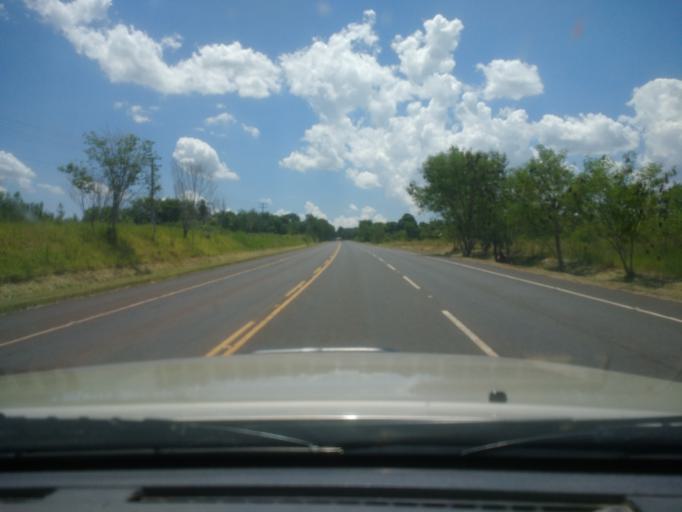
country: PY
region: San Pedro
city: Guayaybi
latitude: -24.5979
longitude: -56.5052
